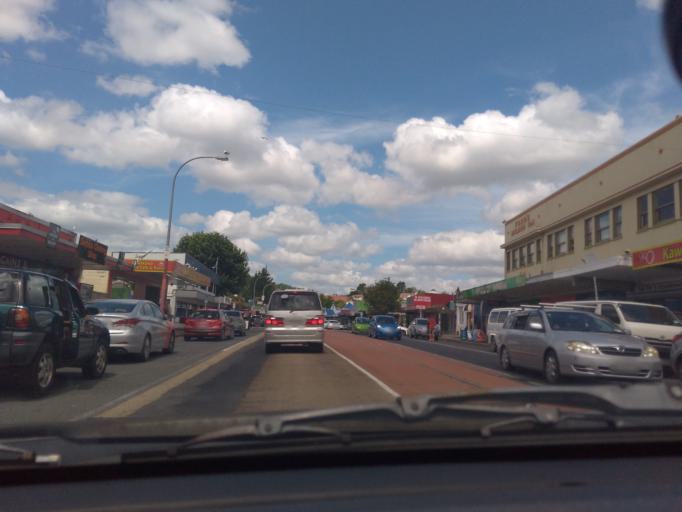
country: NZ
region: Northland
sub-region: Far North District
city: Kawakawa
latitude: -35.3800
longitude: 174.0662
